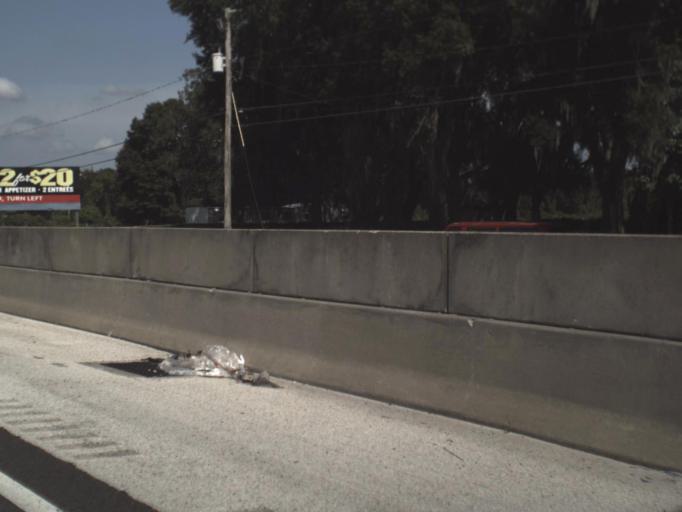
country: US
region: Florida
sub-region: Hillsborough County
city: Plant City
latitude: 28.0370
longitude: -82.0904
